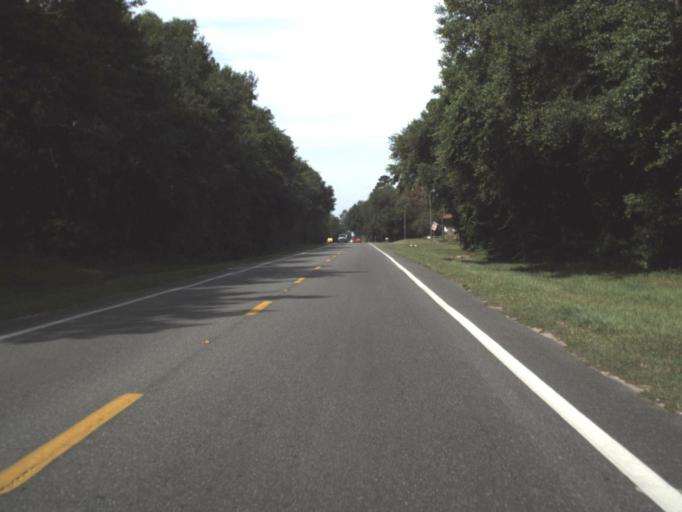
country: US
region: Florida
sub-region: Suwannee County
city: Live Oak
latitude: 30.2634
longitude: -83.0272
